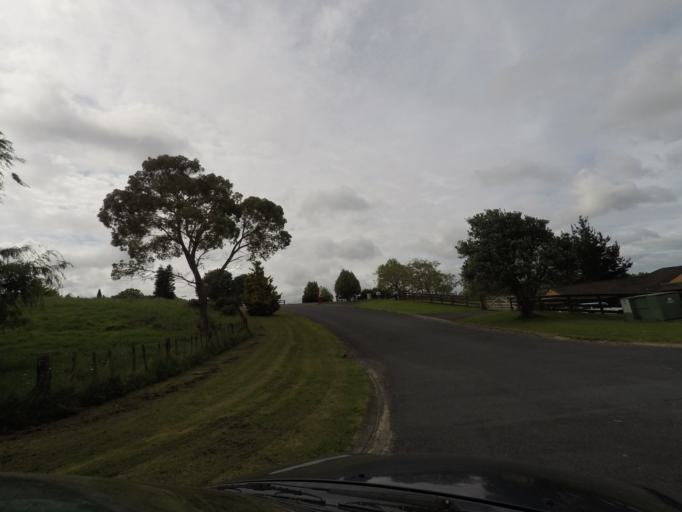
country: NZ
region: Auckland
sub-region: Auckland
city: Muriwai Beach
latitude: -36.7588
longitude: 174.5612
